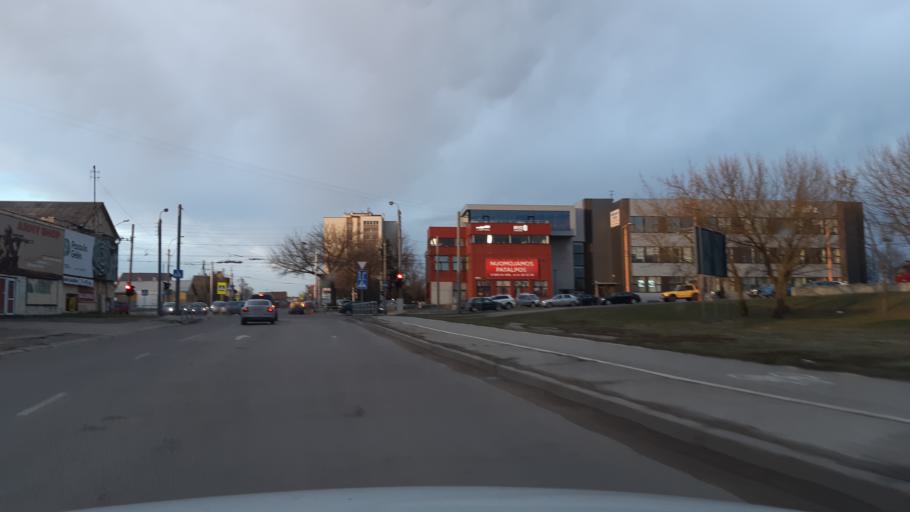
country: LT
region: Kauno apskritis
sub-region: Kaunas
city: Kaunas
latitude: 54.9036
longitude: 23.8875
